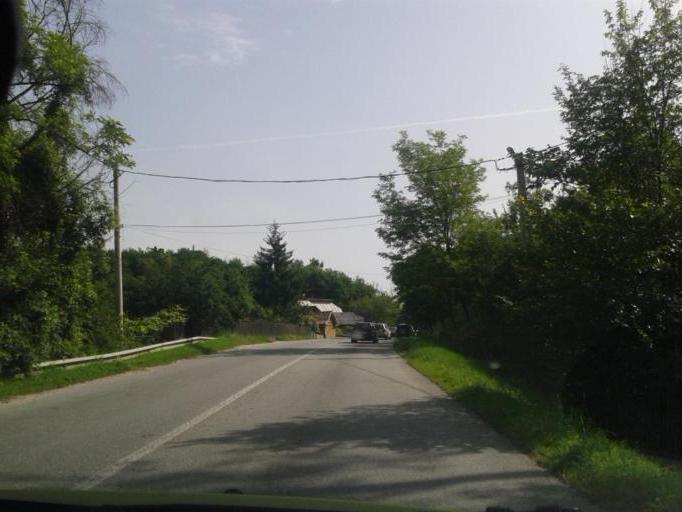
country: RO
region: Valcea
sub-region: Comuna Pietrari
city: Pietrari
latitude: 45.1005
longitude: 24.1322
